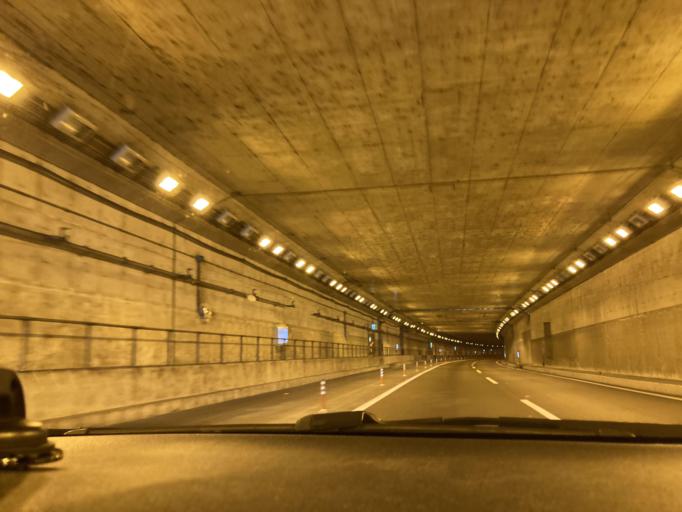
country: JP
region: Okinawa
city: Naha-shi
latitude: 26.2179
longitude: 127.6634
